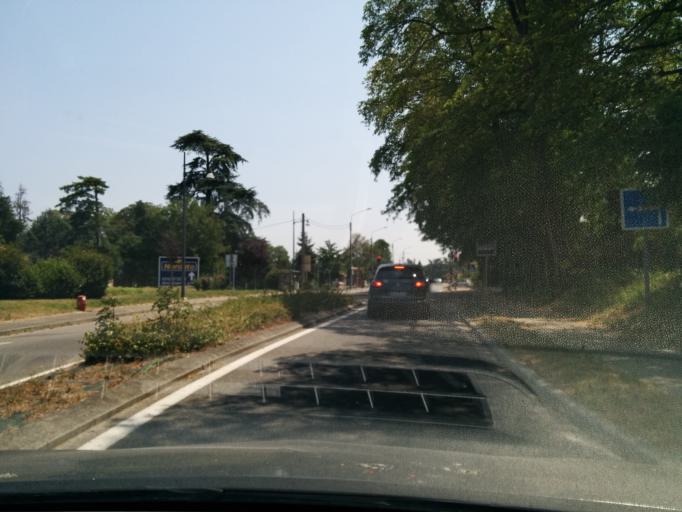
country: FR
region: Midi-Pyrenees
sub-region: Departement de la Haute-Garonne
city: Pompertuzat
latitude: 43.4951
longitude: 1.5202
